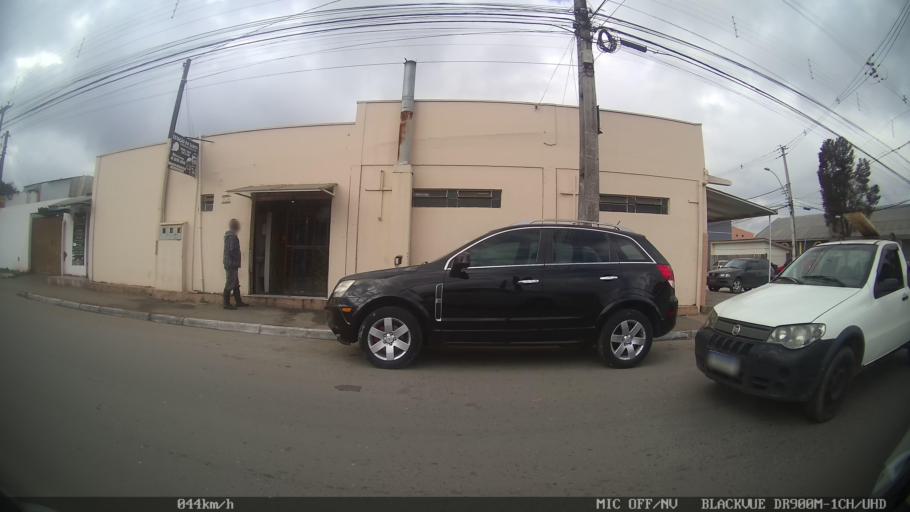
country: BR
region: Parana
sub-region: Colombo
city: Colombo
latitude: -25.3450
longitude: -49.2433
